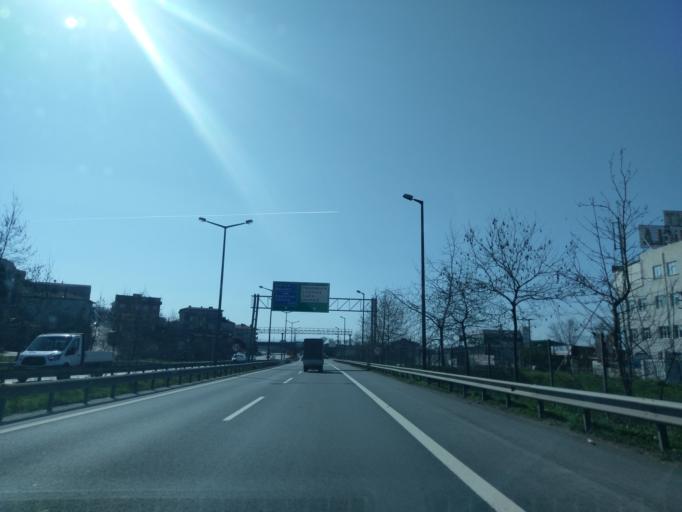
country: TR
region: Kocaeli
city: Darica
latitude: 40.8211
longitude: 29.3647
